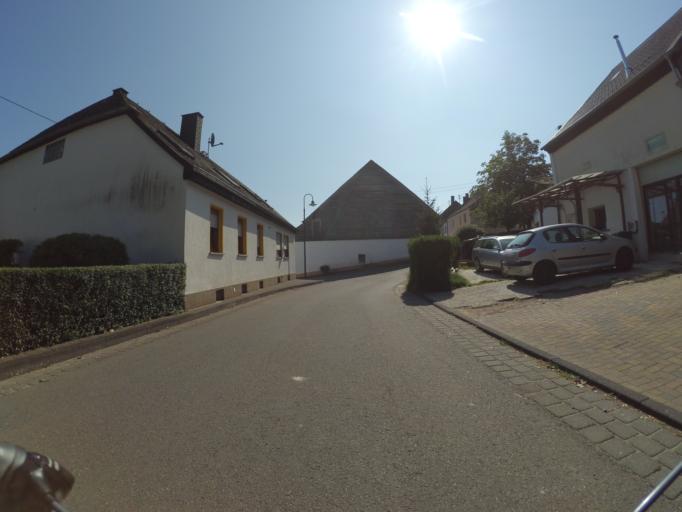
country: DE
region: Rheinland-Pfalz
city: Gielert
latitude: 49.7745
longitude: 7.0021
